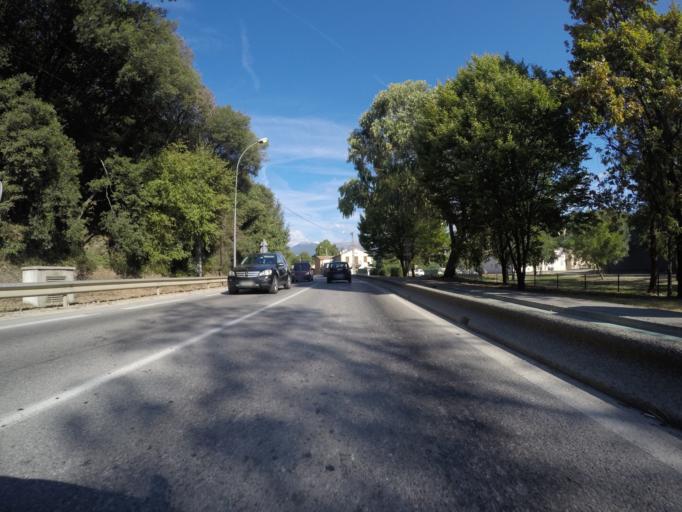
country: FR
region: Provence-Alpes-Cote d'Azur
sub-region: Departement des Alpes-Maritimes
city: Villeneuve-Loubet
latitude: 43.6550
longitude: 7.1247
